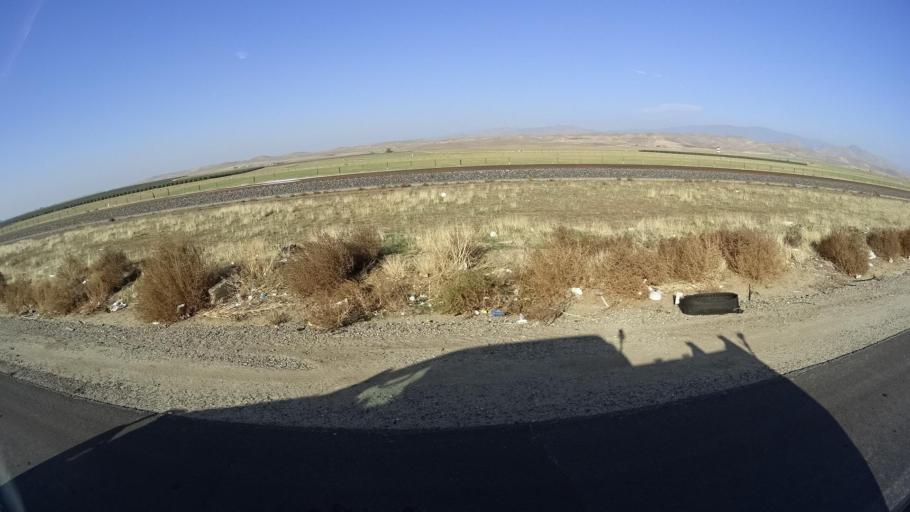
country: US
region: California
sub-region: Kern County
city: Lamont
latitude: 35.3354
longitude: -118.8193
